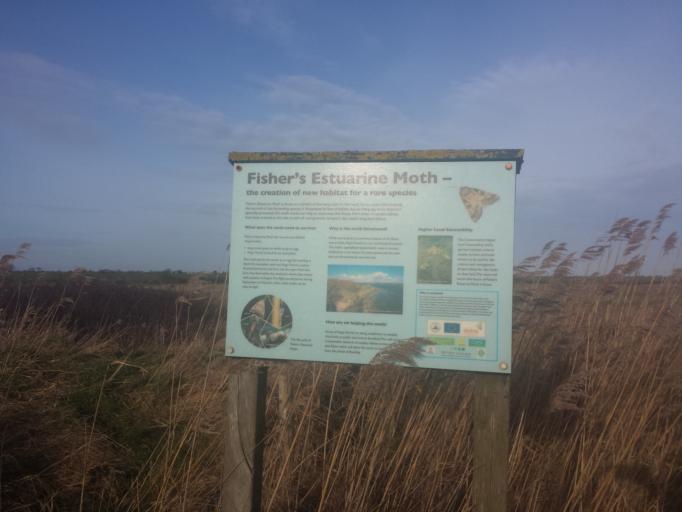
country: GB
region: England
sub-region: Essex
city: Frinton-on-Sea
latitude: 51.8126
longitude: 1.2215
